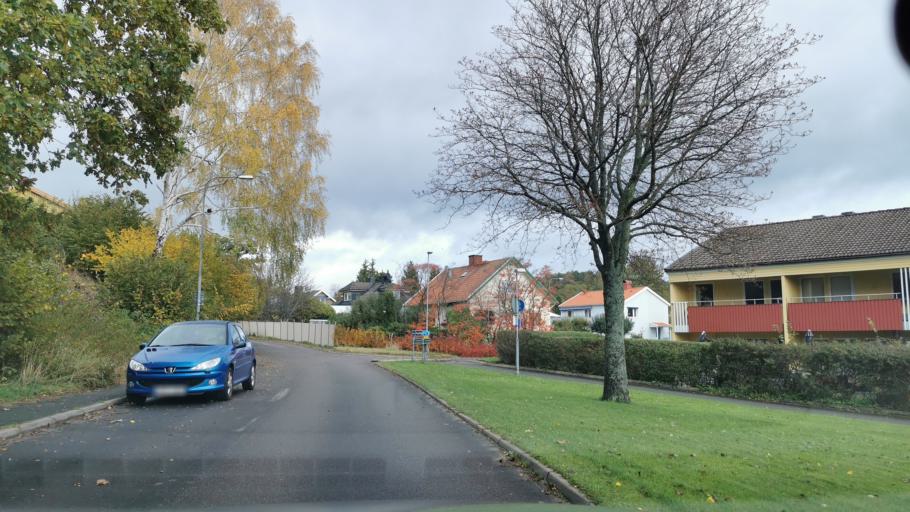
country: SE
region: Vaestra Goetaland
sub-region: Partille Kommun
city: Partille
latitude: 57.7256
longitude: 12.0883
